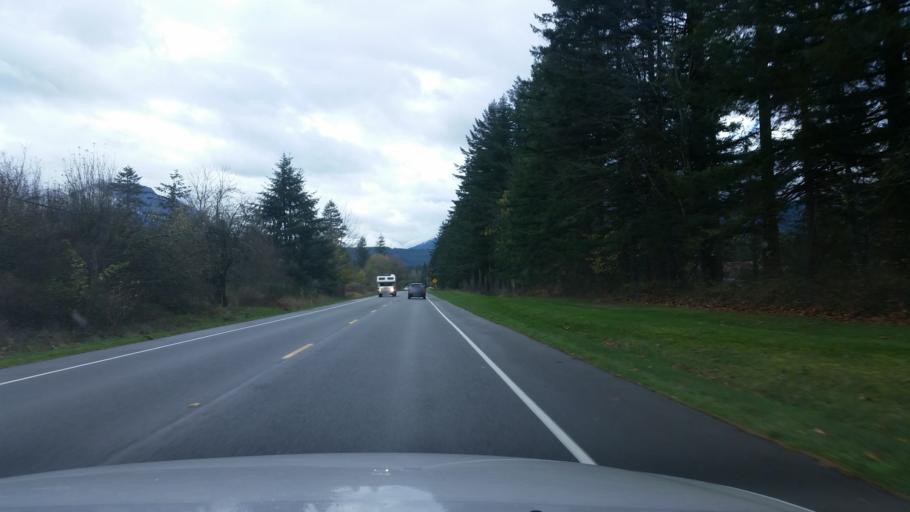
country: US
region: Washington
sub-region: King County
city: Tanner
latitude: 47.4798
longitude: -121.7549
